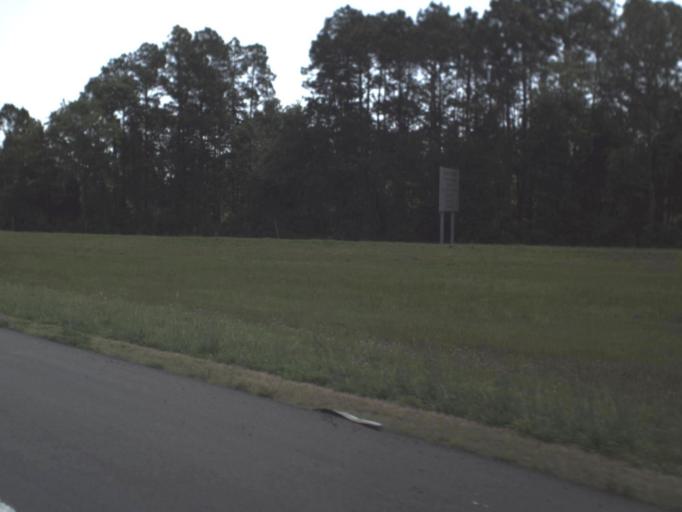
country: US
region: Georgia
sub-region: Camden County
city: Kingsland
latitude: 30.7135
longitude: -81.6702
